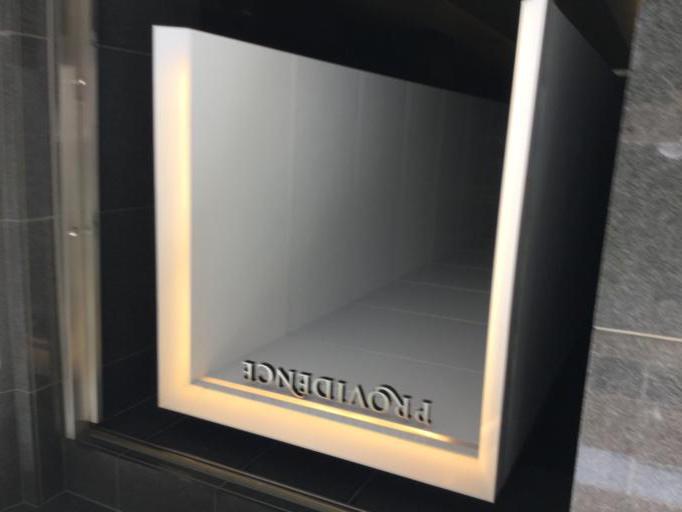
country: JP
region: Hokkaido
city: Sapporo
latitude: 43.0575
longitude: 141.3449
